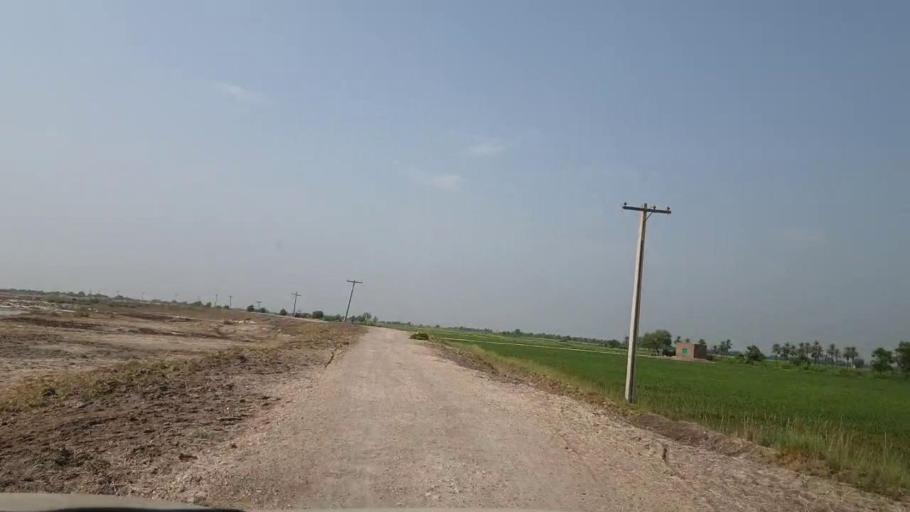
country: PK
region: Sindh
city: Dokri
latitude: 27.4270
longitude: 68.2045
